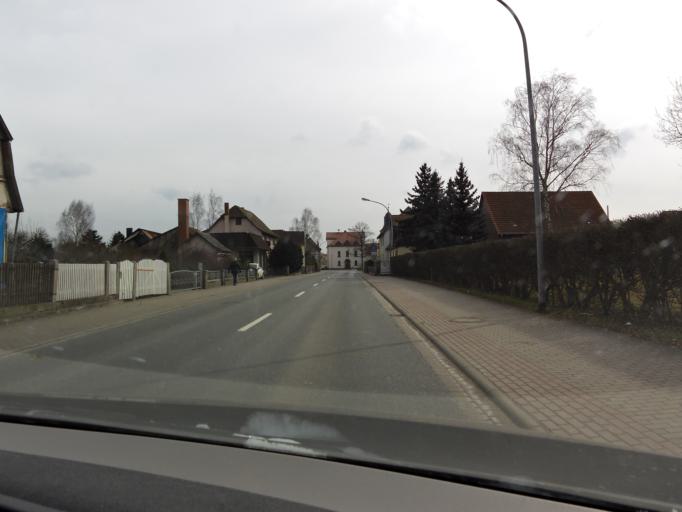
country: DE
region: Thuringia
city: Barchfeld
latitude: 50.8025
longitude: 10.2964
